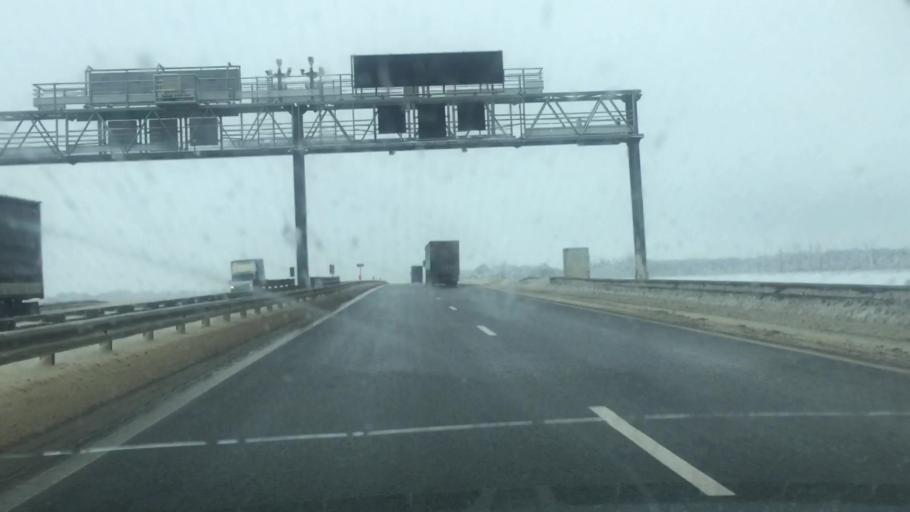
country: RU
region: Lipetsk
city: Stanovoye
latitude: 52.8956
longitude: 38.2300
